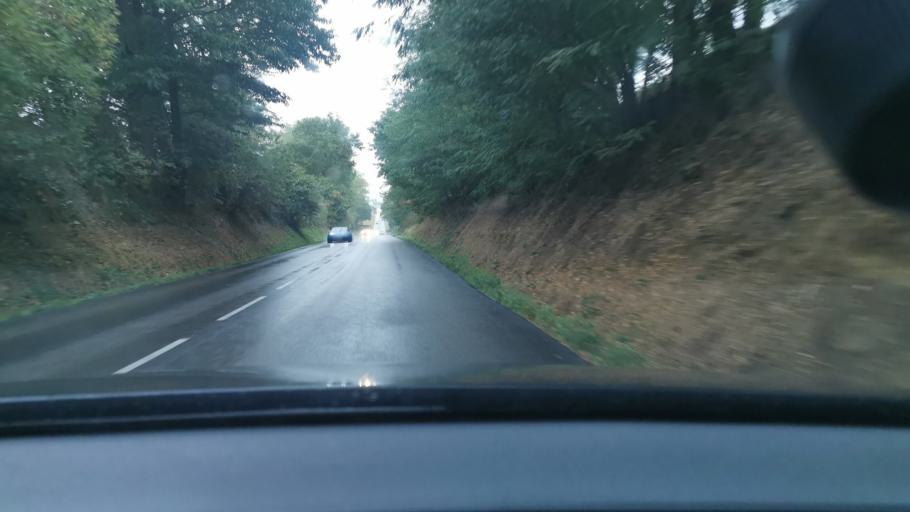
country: FR
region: Rhone-Alpes
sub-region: Departement du Rhone
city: Montanay
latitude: 45.8945
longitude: 4.8813
